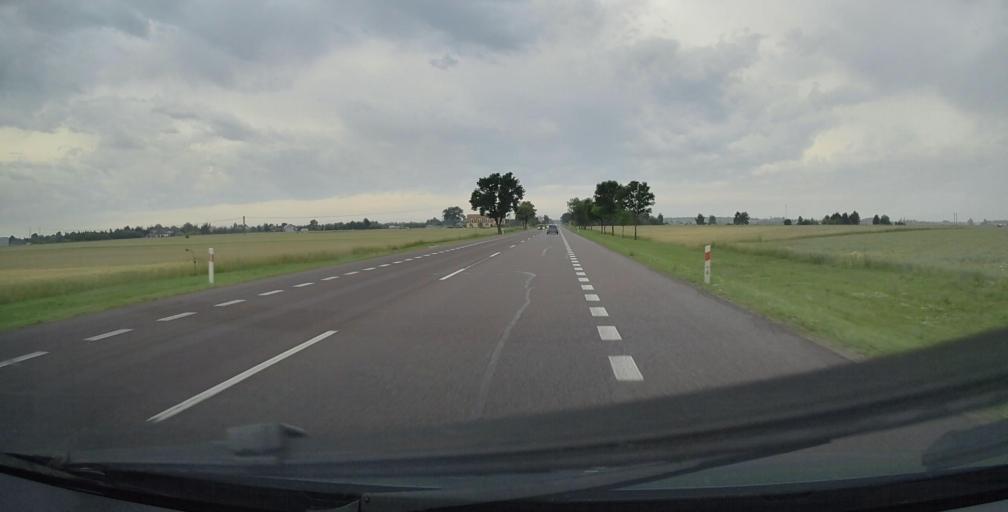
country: PL
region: Lublin Voivodeship
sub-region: Powiat bialski
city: Miedzyrzec Podlaski
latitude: 52.0000
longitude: 22.7938
